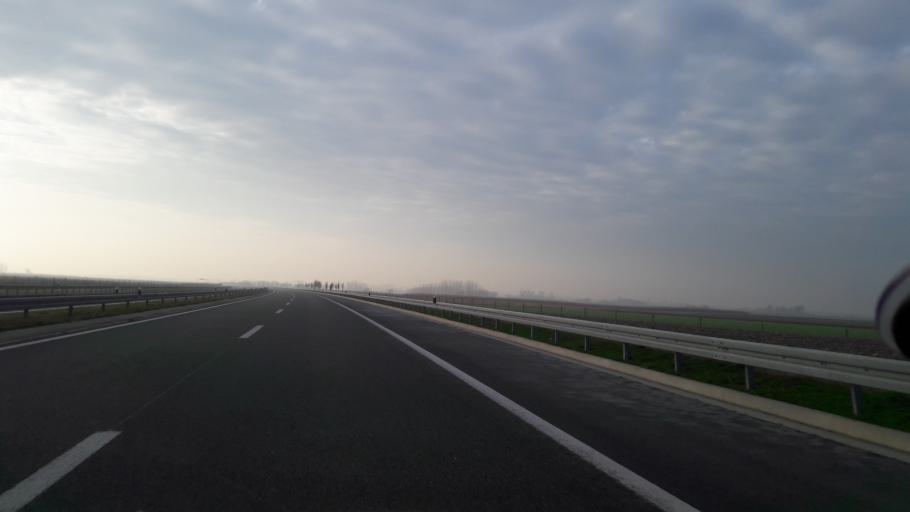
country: HR
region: Osjecko-Baranjska
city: Gorjani
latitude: 45.3771
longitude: 18.3949
